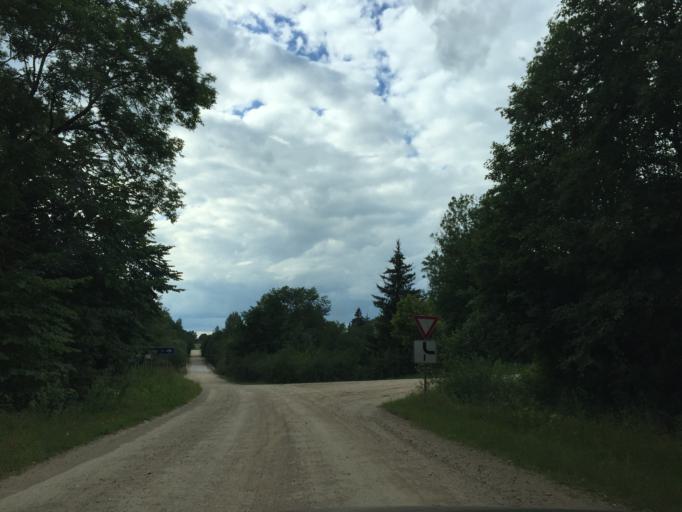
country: LV
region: Malpils
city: Malpils
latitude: 56.9630
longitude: 24.9837
